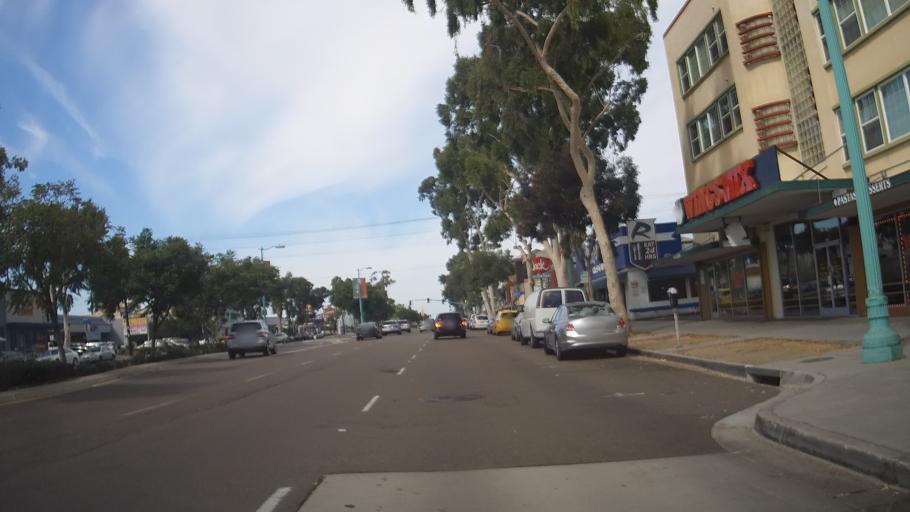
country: US
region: California
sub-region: San Diego County
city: San Diego
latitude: 32.7555
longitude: -117.1305
